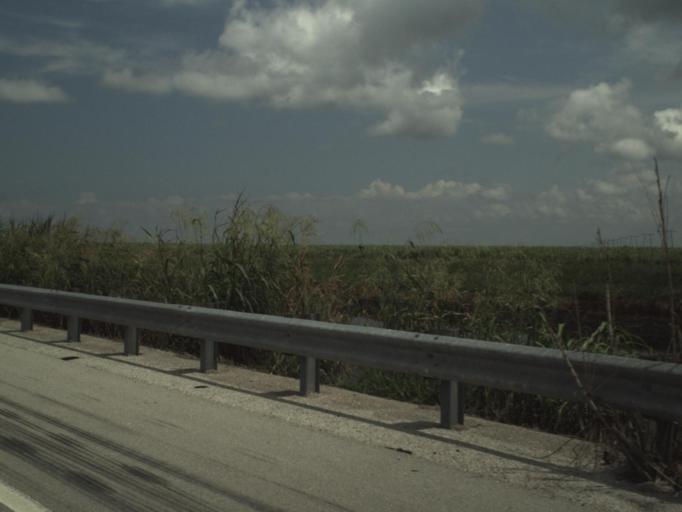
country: US
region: Florida
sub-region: Palm Beach County
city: Pahokee
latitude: 26.8270
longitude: -80.5821
